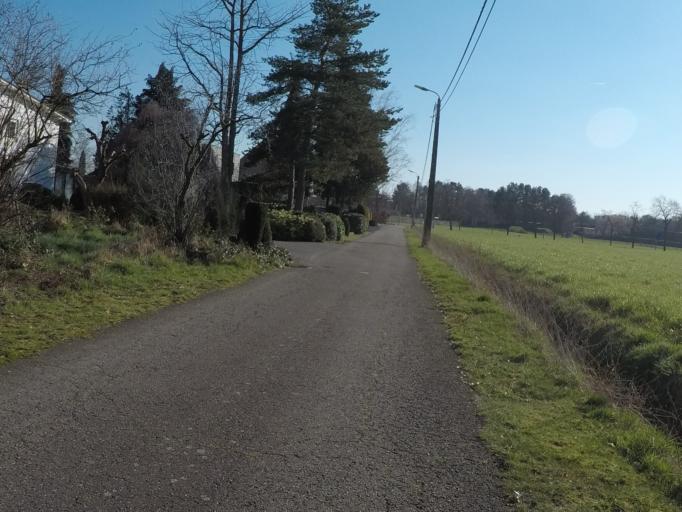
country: BE
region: Flanders
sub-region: Provincie Antwerpen
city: Heist-op-den-Berg
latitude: 51.0726
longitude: 4.7420
